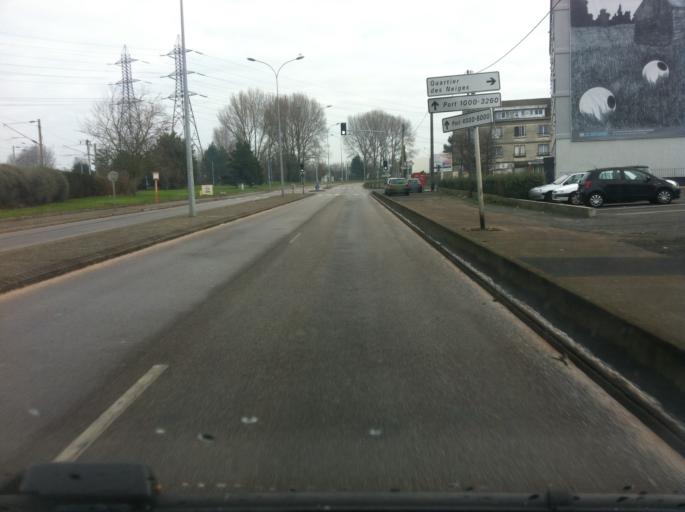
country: FR
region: Haute-Normandie
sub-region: Departement de la Seine-Maritime
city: Harfleur
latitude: 49.4823
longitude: 0.1610
